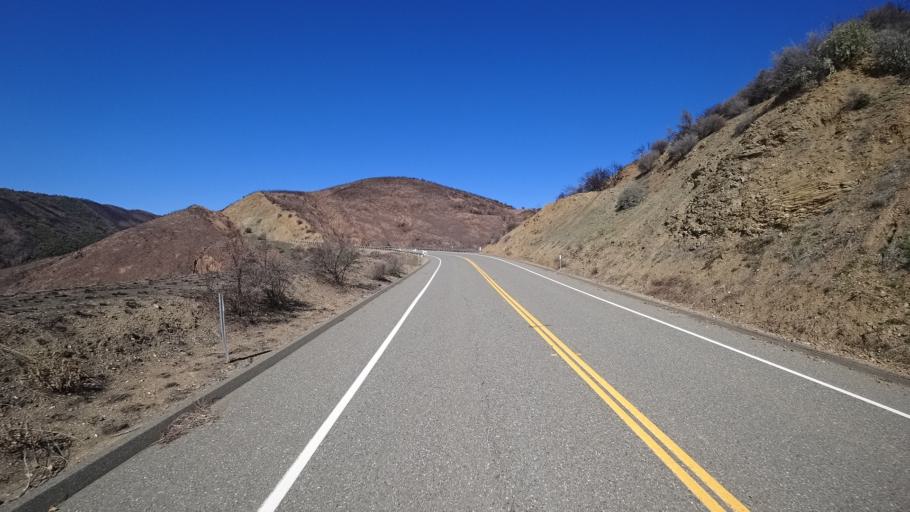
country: US
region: California
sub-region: Tehama County
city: Rancho Tehama Reserve
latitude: 39.6626
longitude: -122.6372
